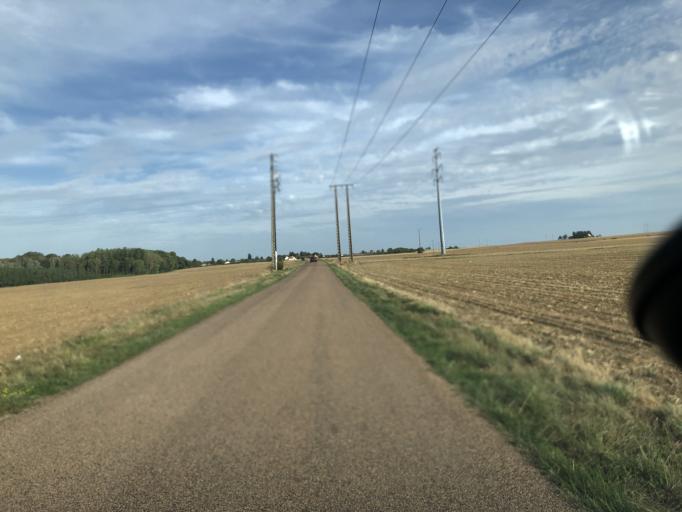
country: FR
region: Bourgogne
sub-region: Departement de l'Yonne
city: Joigny
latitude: 47.9621
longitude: 3.3842
